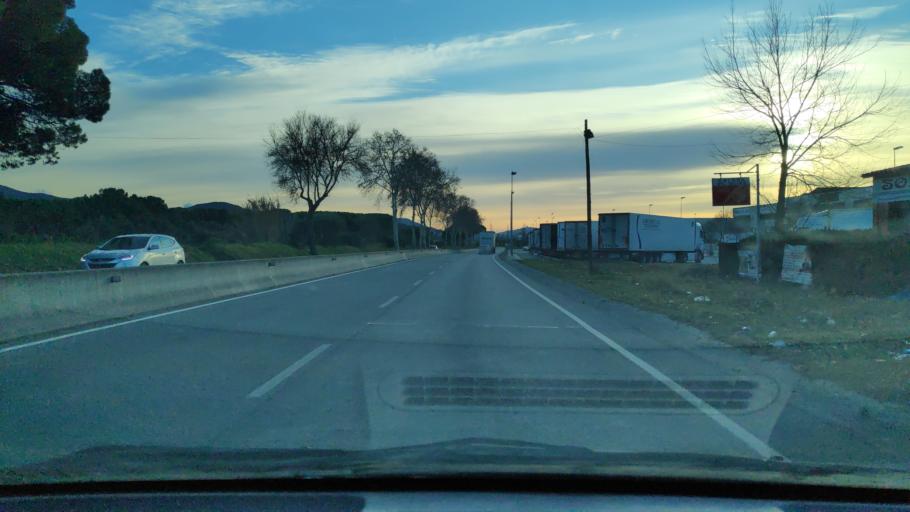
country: ES
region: Catalonia
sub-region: Provincia de Barcelona
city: Montmelo
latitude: 41.5692
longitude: 2.2682
